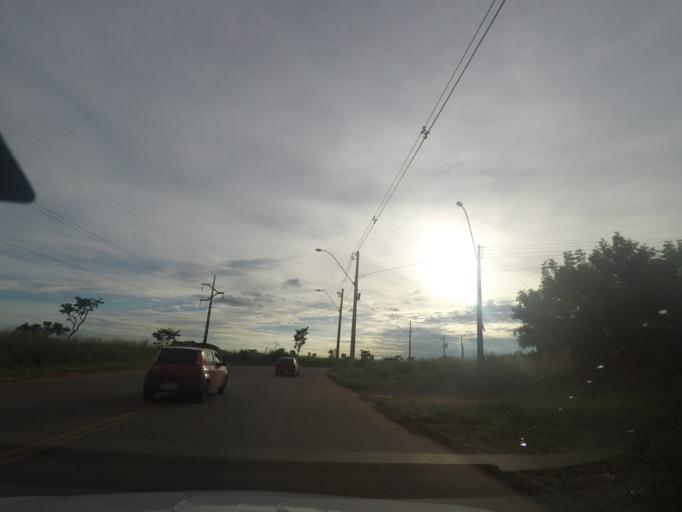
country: BR
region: Goias
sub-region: Trindade
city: Trindade
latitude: -16.7164
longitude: -49.3849
